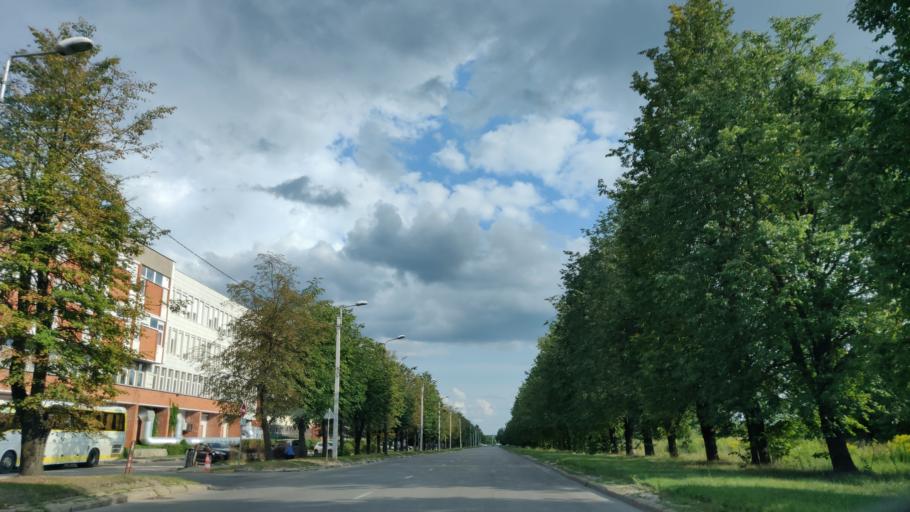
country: LT
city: Baltoji Voke
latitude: 54.6245
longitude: 25.1408
